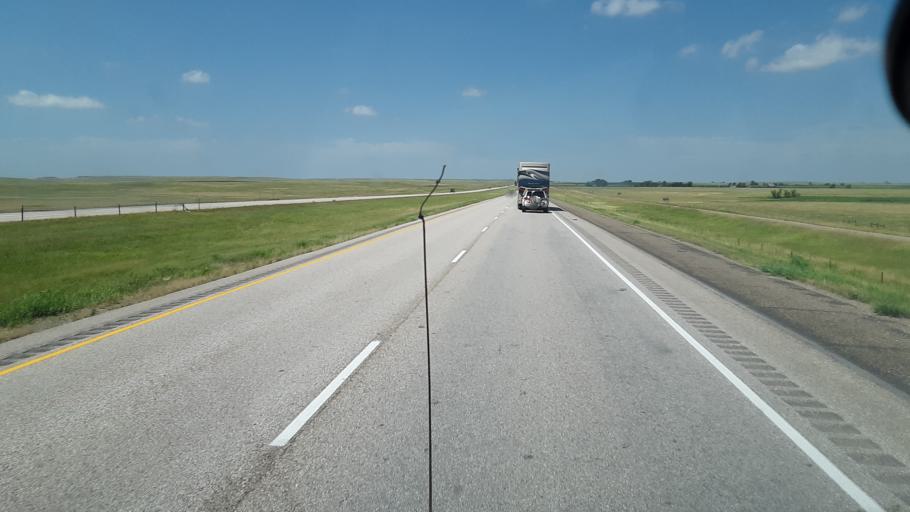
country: US
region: South Dakota
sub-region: Jackson County
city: Kadoka
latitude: 43.8363
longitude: -101.6026
